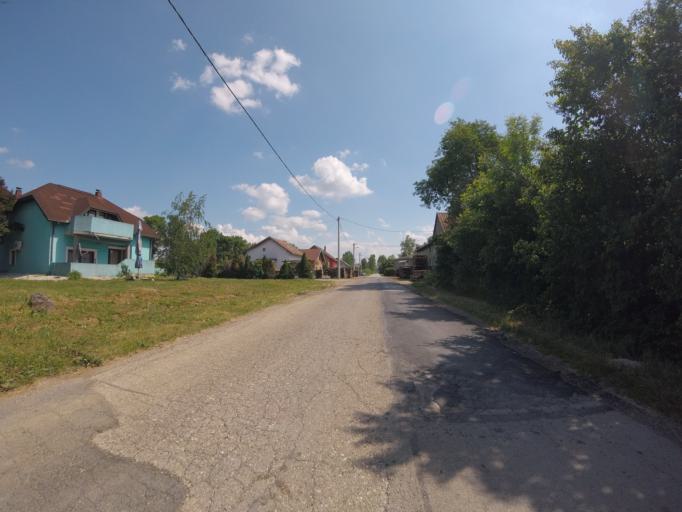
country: HR
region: Zagrebacka
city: Kuce
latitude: 45.6751
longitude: 16.1827
